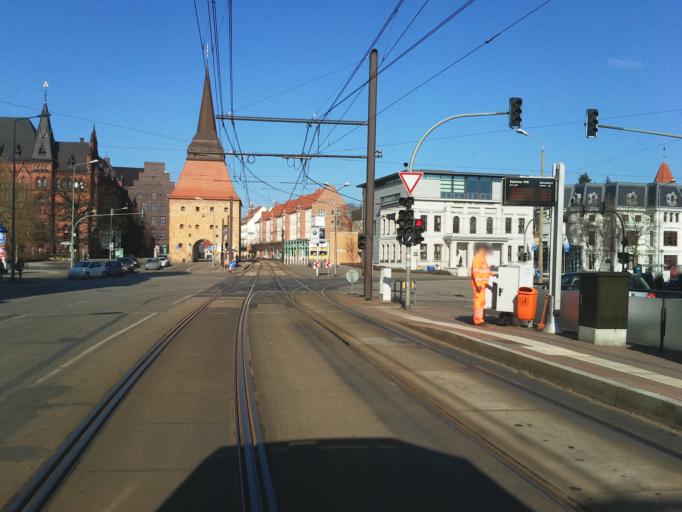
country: DE
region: Mecklenburg-Vorpommern
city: Rostock
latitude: 54.0854
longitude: 12.1412
